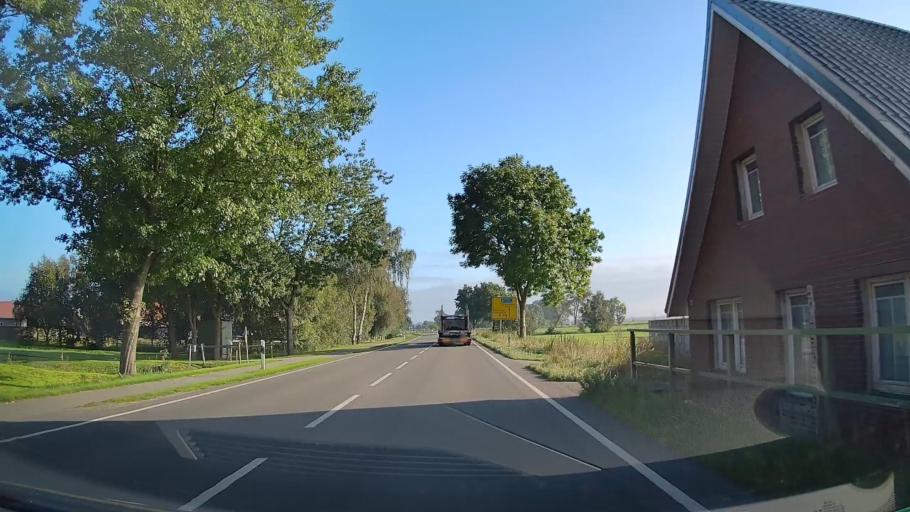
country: DE
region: Lower Saxony
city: Ovelgonne
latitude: 53.2794
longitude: 8.3669
